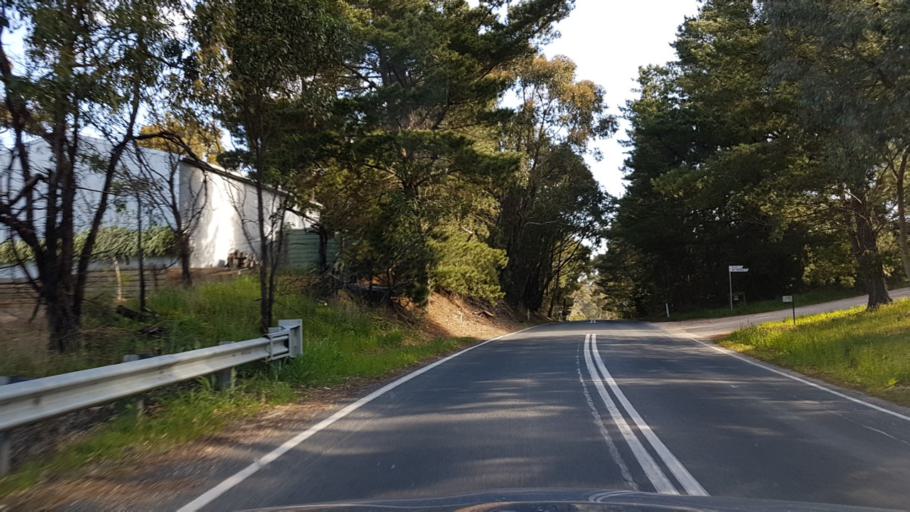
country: AU
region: South Australia
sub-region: Adelaide Hills
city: Lobethal
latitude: -34.8788
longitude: 138.8918
